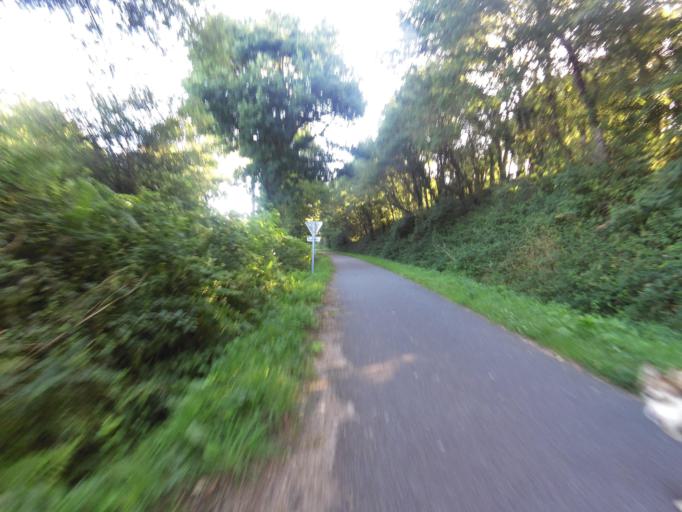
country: FR
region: Brittany
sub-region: Departement du Morbihan
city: Guillac
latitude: 47.9046
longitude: -2.4326
